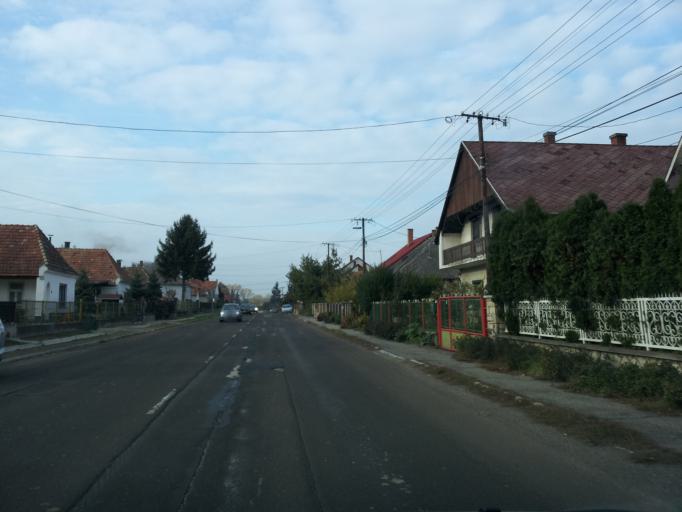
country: HU
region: Gyor-Moson-Sopron
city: Pannonhalma
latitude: 47.5220
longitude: 17.7493
